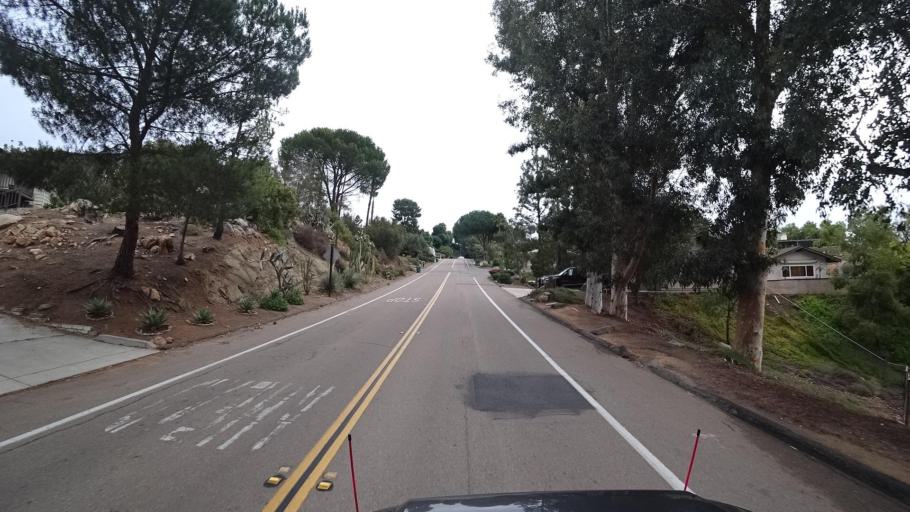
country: US
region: California
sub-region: San Diego County
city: Rancho San Diego
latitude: 32.7720
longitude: -116.9169
